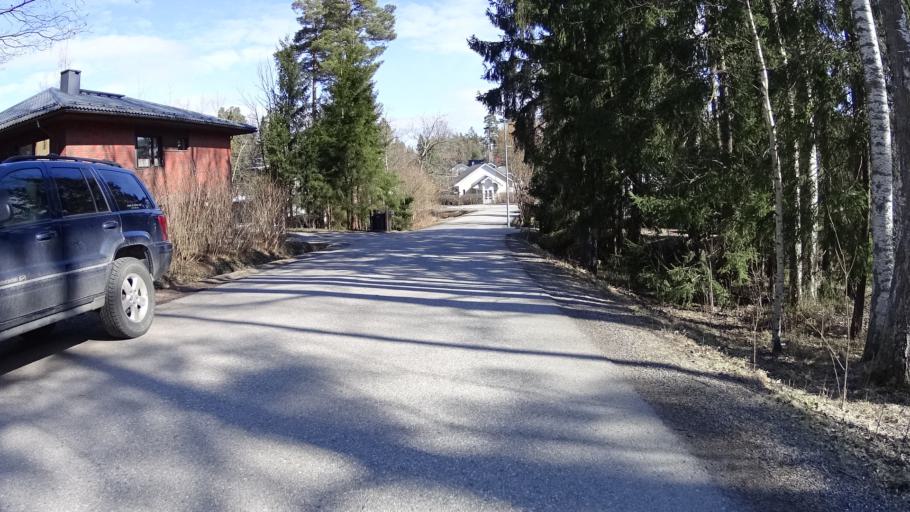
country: FI
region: Uusimaa
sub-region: Helsinki
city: Kauniainen
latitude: 60.2170
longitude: 24.7379
